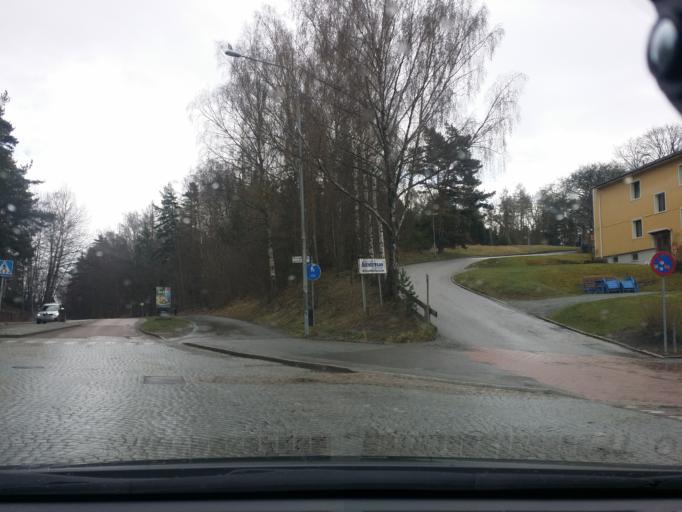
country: SE
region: Uppsala
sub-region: Enkopings Kommun
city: Enkoping
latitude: 59.6439
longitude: 17.0874
